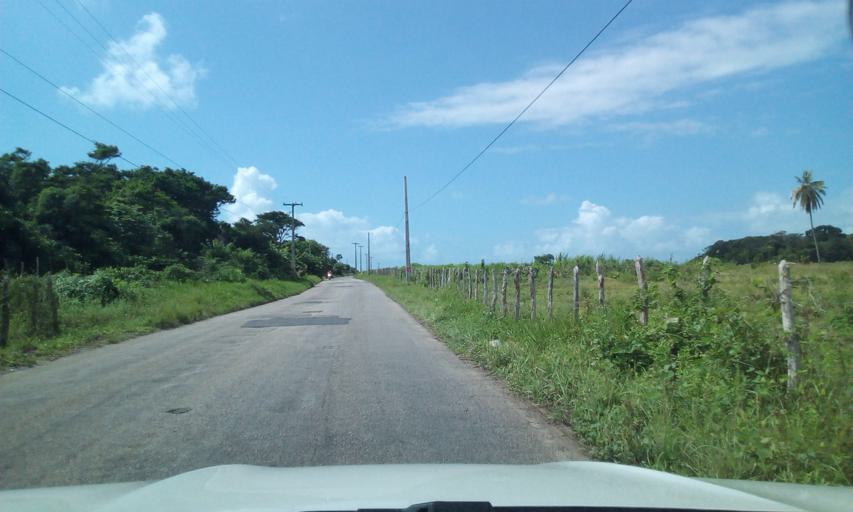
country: BR
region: Paraiba
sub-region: Conde
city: Conde
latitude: -7.2212
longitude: -34.8305
